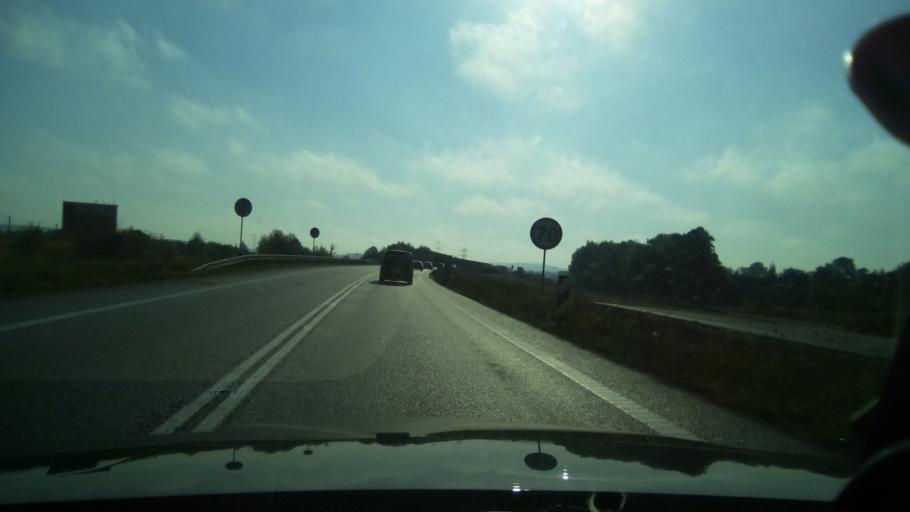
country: PL
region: Silesian Voivodeship
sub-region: Powiat bedzinski
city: Mierzecice
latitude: 50.4249
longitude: 19.1715
